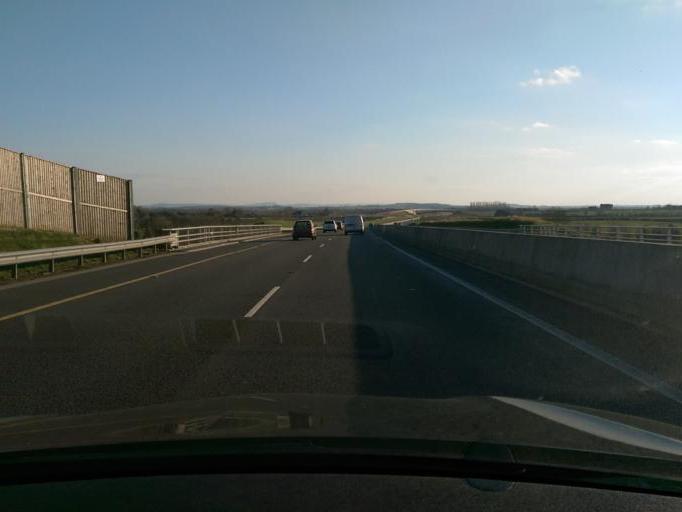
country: IE
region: Leinster
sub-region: Laois
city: Mountrath
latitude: 52.9758
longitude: -7.4327
